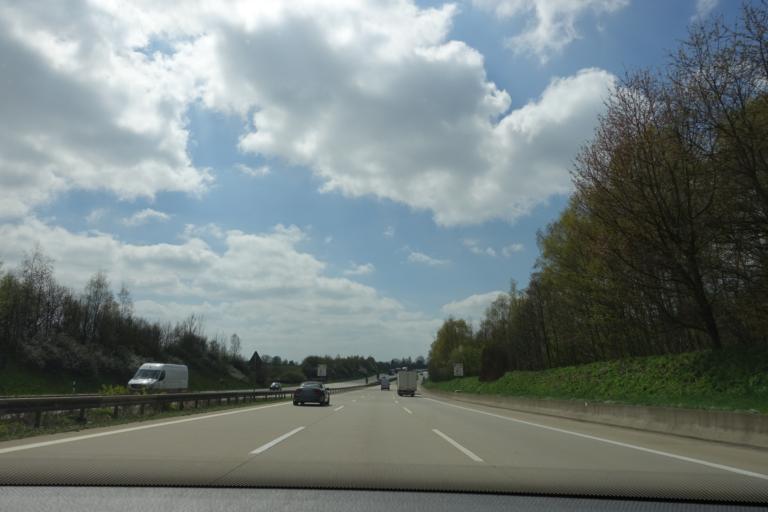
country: DE
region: Saxony
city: Frankenberg
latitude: 50.9328
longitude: 13.0582
